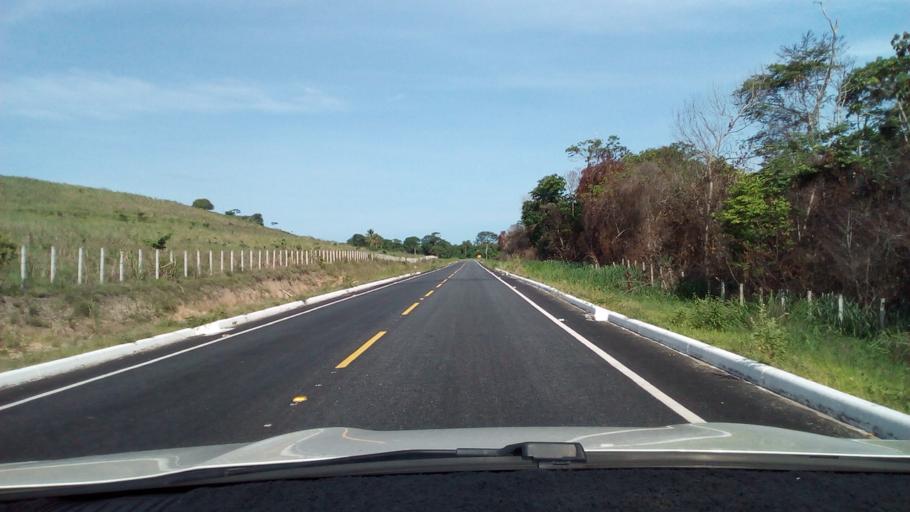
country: BR
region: Paraiba
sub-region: Bayeux
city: Bayeux
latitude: -7.0630
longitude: -34.9227
